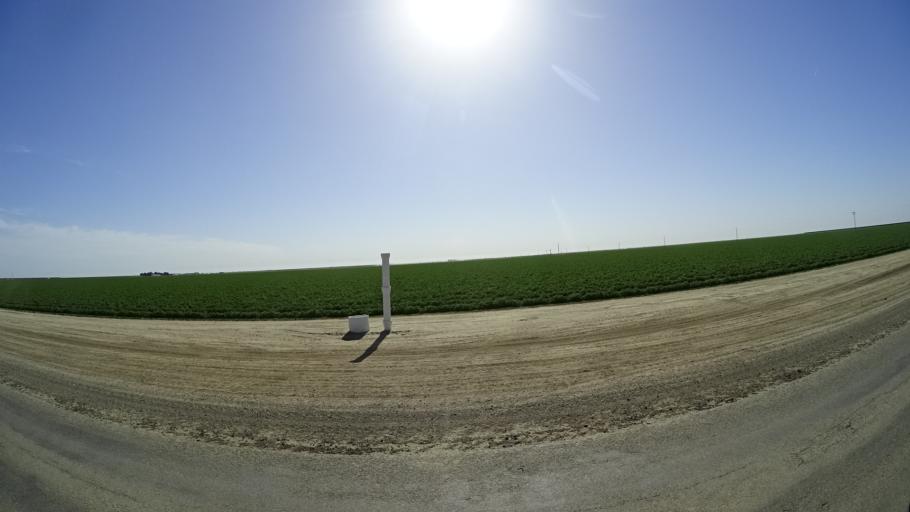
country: US
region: California
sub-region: Kings County
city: Kettleman City
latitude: 36.1253
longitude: -120.0037
